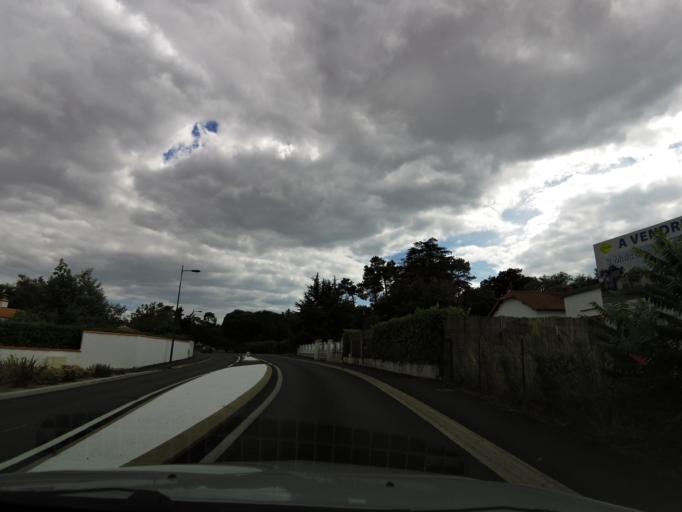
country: FR
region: Pays de la Loire
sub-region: Departement de la Vendee
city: Longeville-sur-Mer
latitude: 46.4104
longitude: -1.4944
